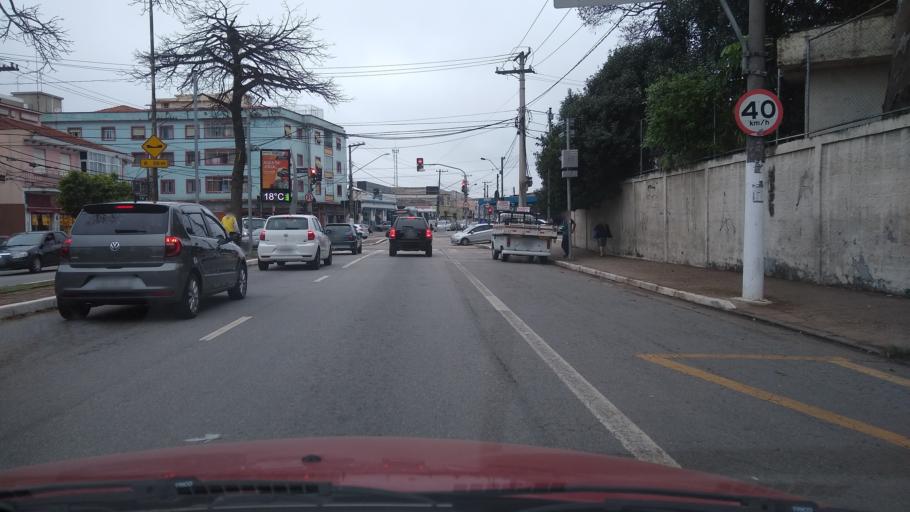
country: BR
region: Sao Paulo
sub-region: Diadema
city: Diadema
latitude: -23.6256
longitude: -46.6194
